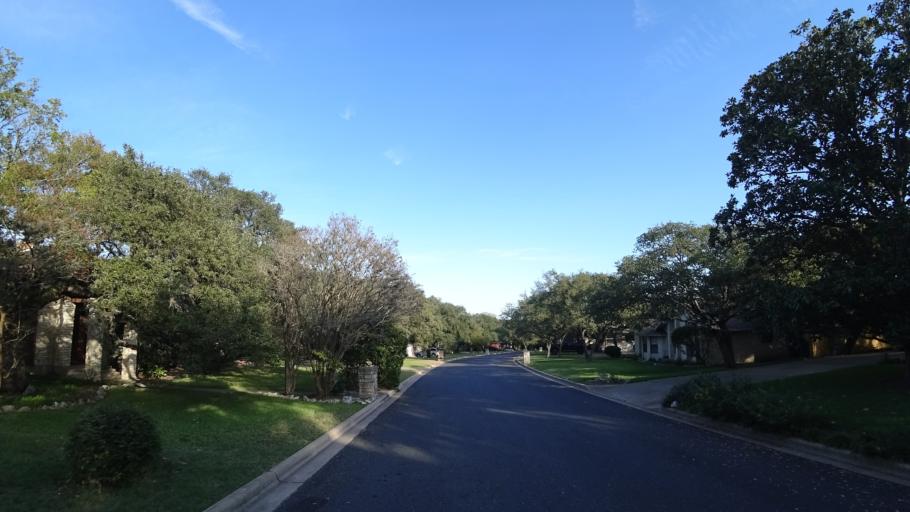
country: US
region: Texas
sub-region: Williamson County
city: Anderson Mill
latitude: 30.4396
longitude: -97.8040
